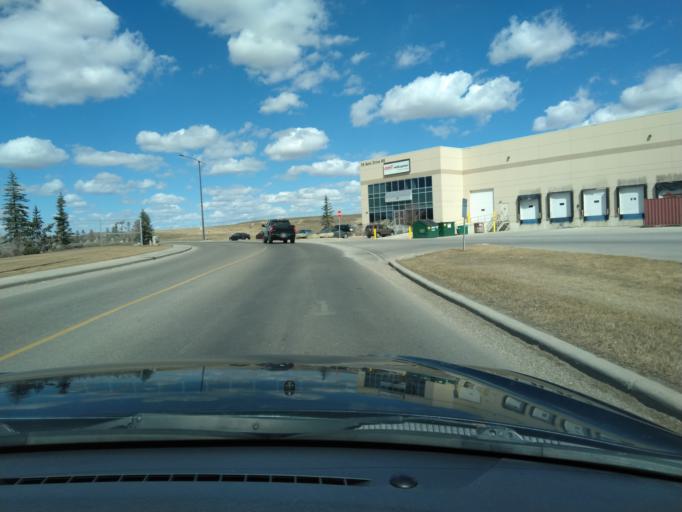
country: CA
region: Alberta
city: Calgary
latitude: 51.1241
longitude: -114.0398
